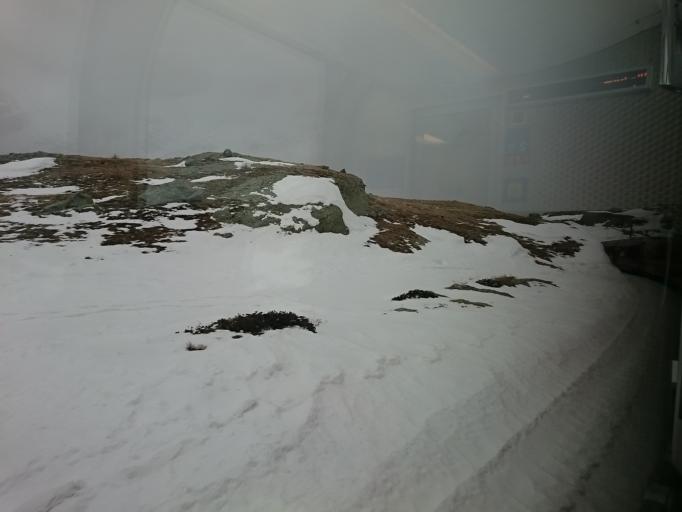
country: CH
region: Grisons
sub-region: Bernina District
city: Poschiavo
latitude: 46.3901
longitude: 10.0318
